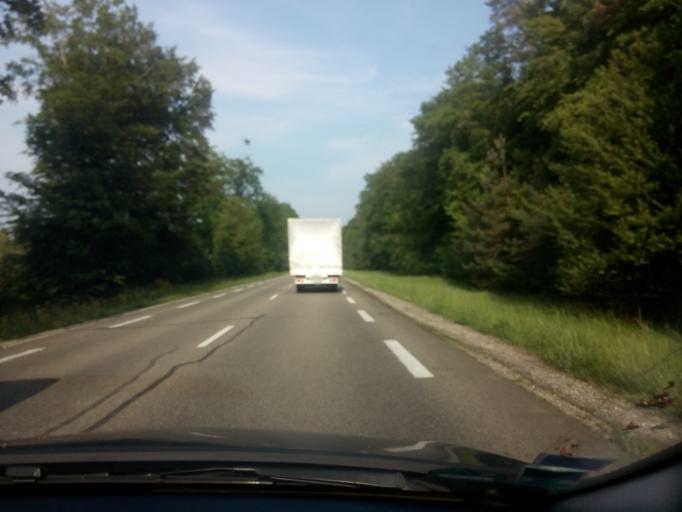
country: FR
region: Alsace
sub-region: Departement du Bas-Rhin
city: Kaltenhouse
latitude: 48.8326
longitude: 7.8437
